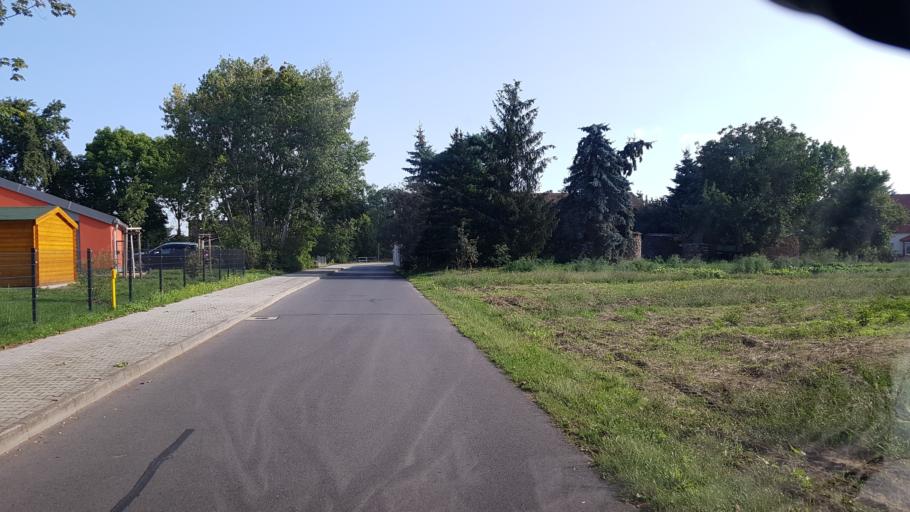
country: DE
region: Brandenburg
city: Luebben
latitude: 51.8958
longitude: 13.8058
